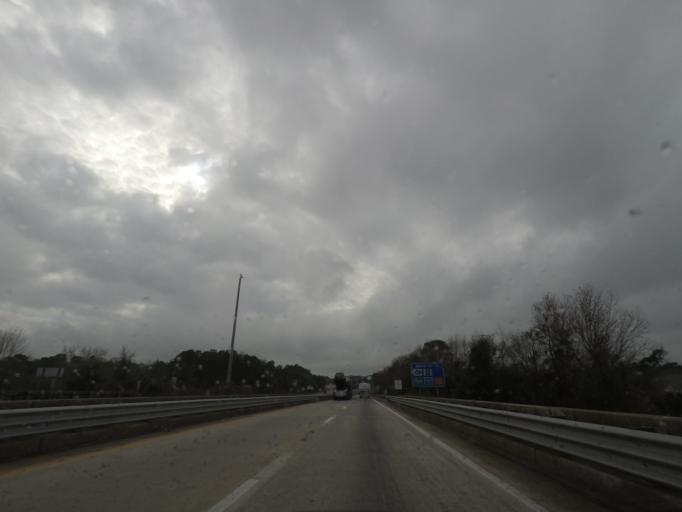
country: US
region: South Carolina
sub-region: Orangeburg County
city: Holly Hill
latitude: 33.5013
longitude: -80.4580
